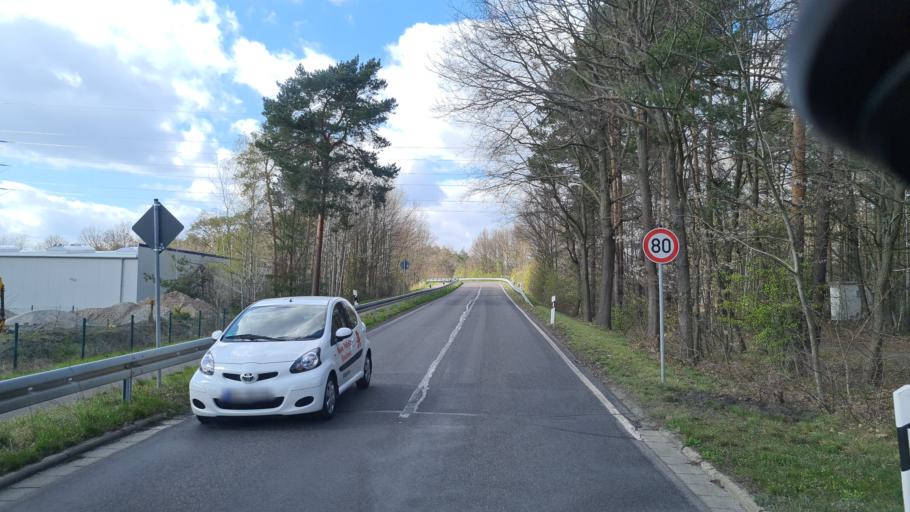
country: DE
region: Brandenburg
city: Schipkau
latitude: 51.5534
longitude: 13.9165
